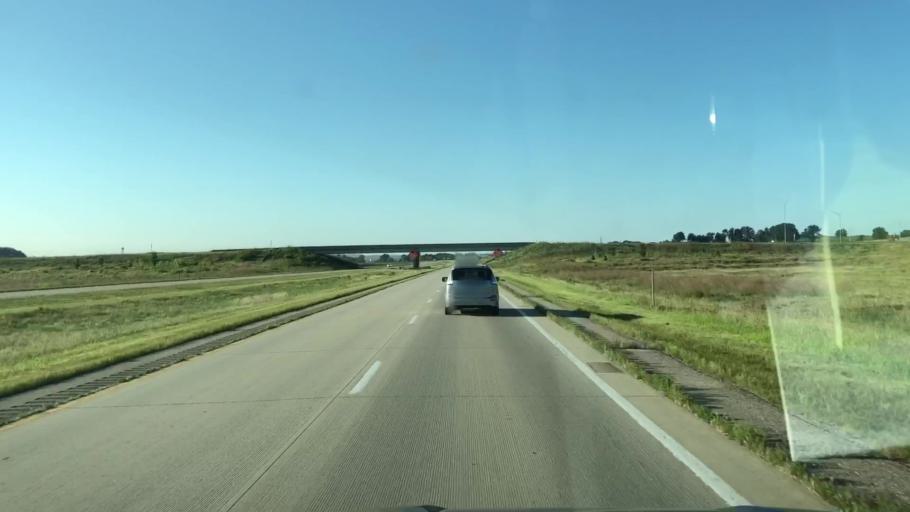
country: US
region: Iowa
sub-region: Plymouth County
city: Le Mars
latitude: 42.7667
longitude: -96.2095
